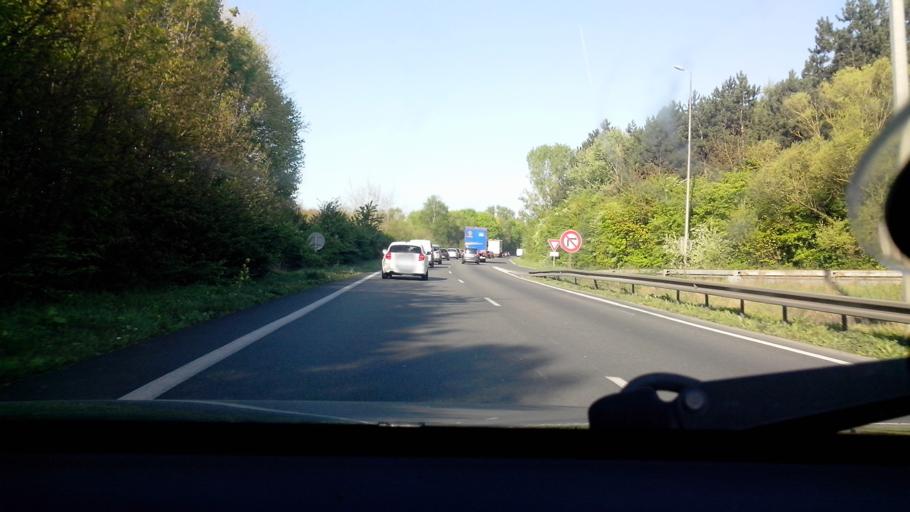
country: FR
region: Ile-de-France
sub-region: Departement de l'Essonne
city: Bondoufle
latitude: 48.6237
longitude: 2.3889
